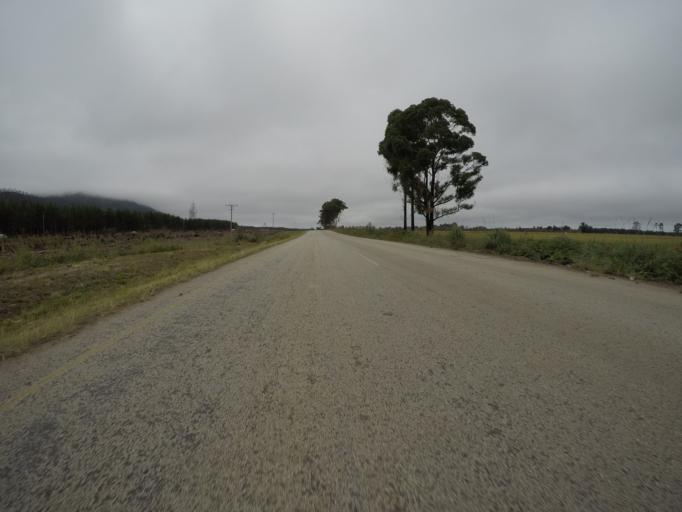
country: ZA
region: Eastern Cape
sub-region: Cacadu District Municipality
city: Kareedouw
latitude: -33.9836
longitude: 24.0584
